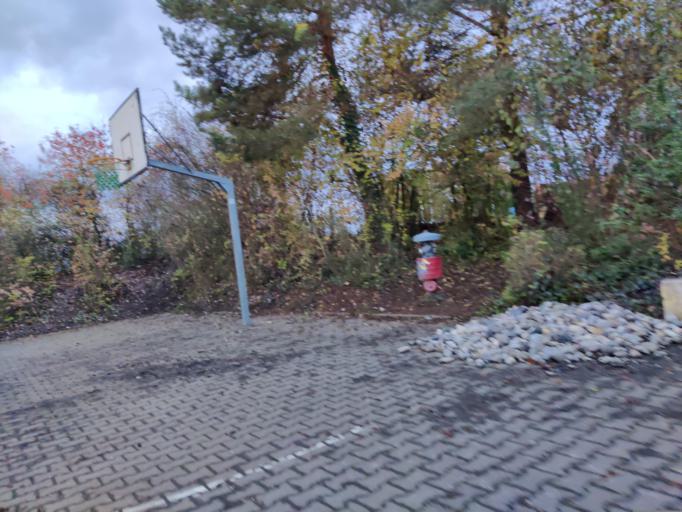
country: DE
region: Baden-Wuerttemberg
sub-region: Tuebingen Region
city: Nehren
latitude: 48.4461
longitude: 9.0761
